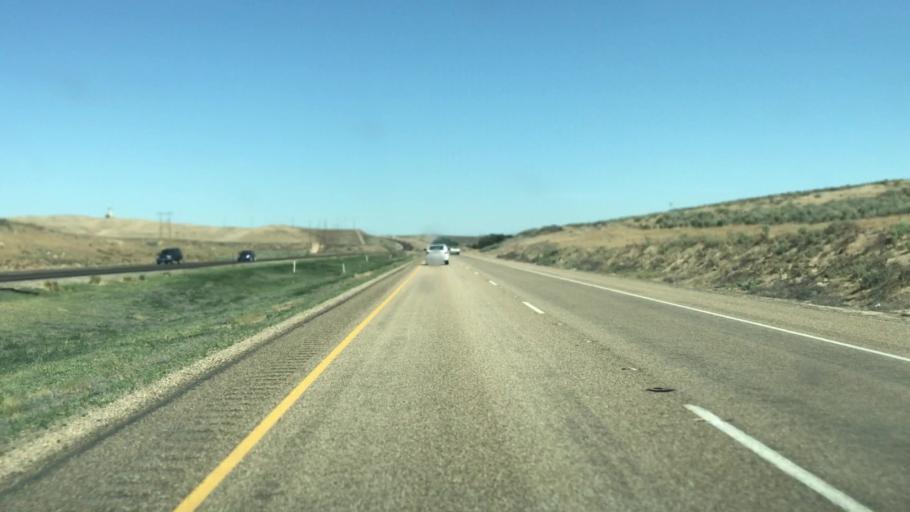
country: US
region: Idaho
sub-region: Payette County
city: New Plymouth
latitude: 43.8903
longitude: -116.8041
